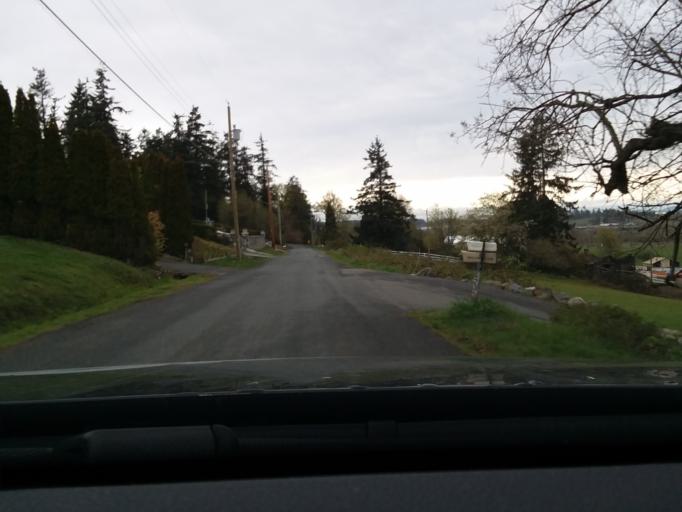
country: CA
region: British Columbia
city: North Saanich
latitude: 48.5524
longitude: -123.3900
